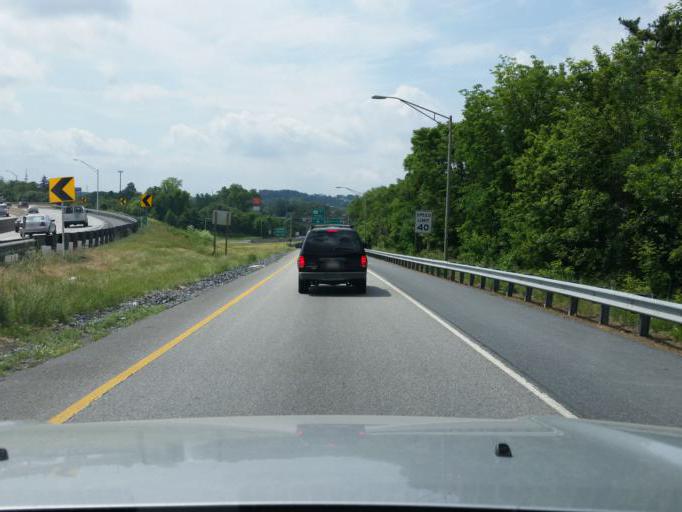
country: US
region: Pennsylvania
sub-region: Dauphin County
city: Lawnton
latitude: 40.2613
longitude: -76.8144
